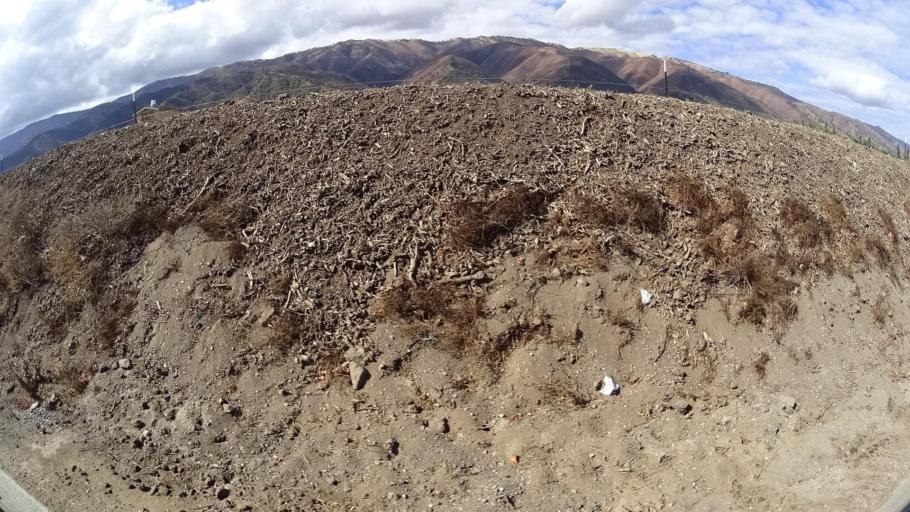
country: US
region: California
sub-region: Monterey County
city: Gonzales
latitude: 36.4882
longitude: -121.4895
